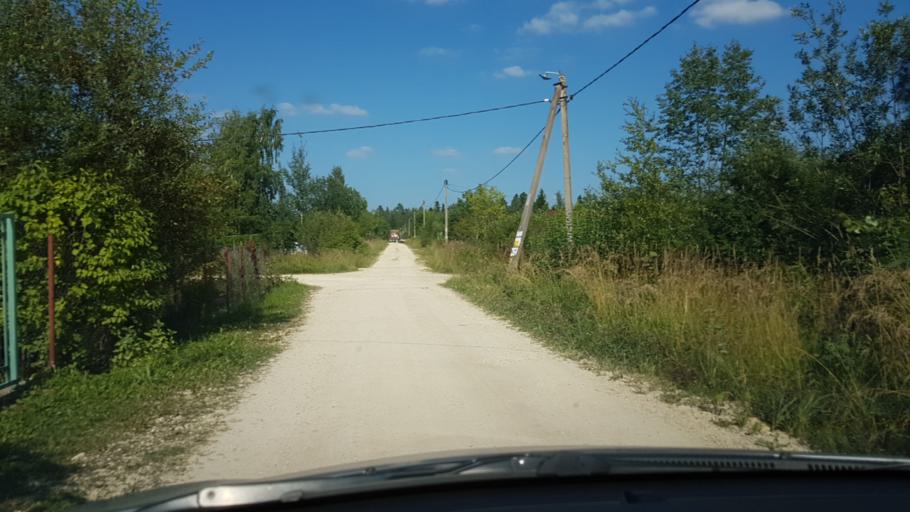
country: RU
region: Leningrad
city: Vyritsa
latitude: 59.4519
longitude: 30.2996
